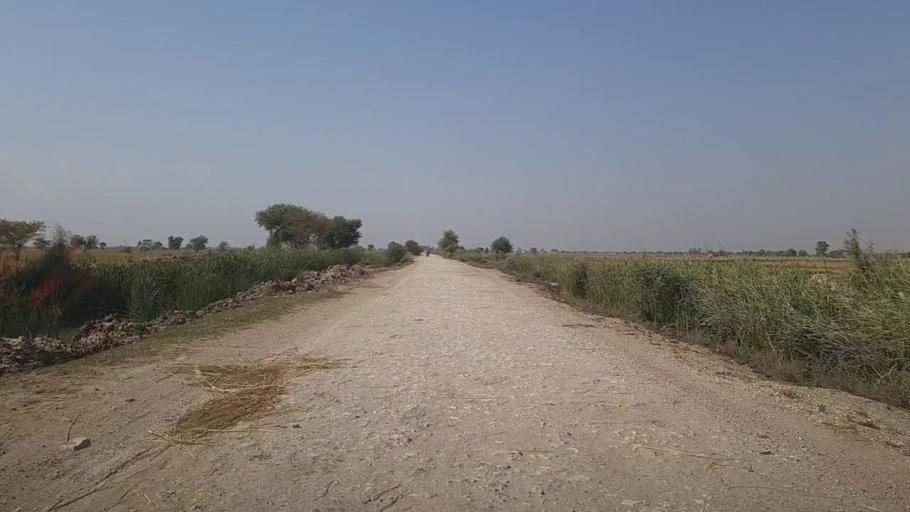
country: PK
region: Sindh
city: Kandhkot
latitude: 28.3984
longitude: 69.2681
